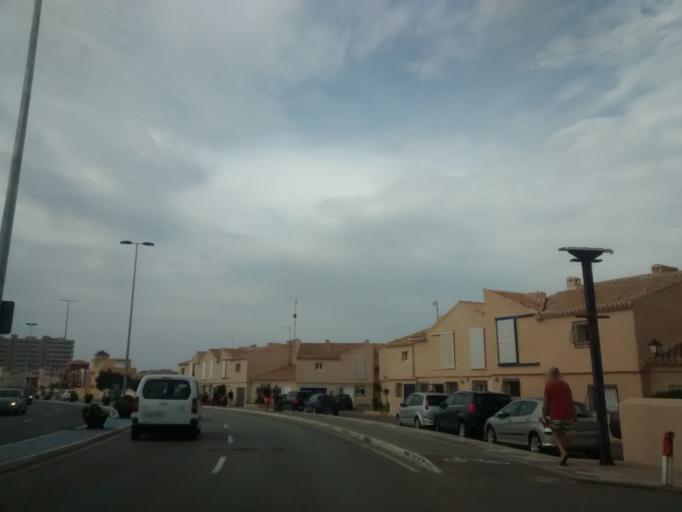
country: ES
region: Murcia
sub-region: Murcia
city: La Manga del Mar Menor
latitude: 37.6736
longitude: -0.7304
